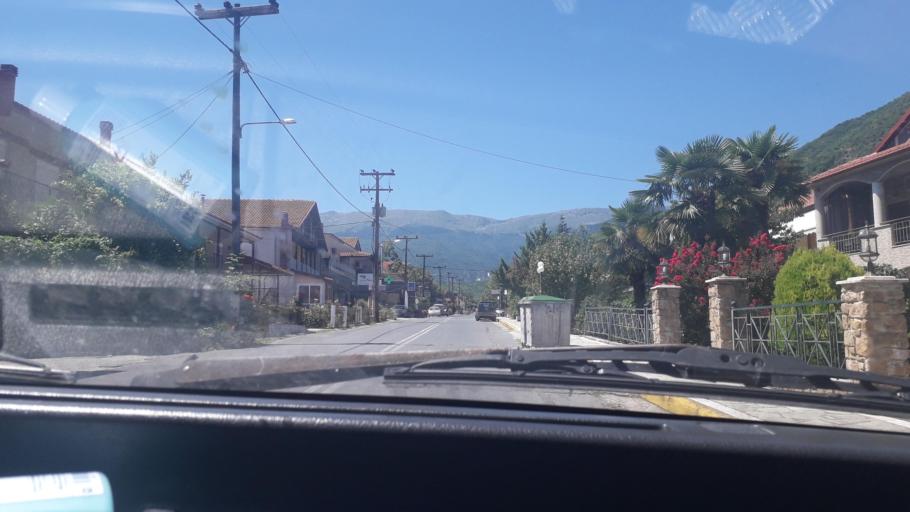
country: GR
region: Central Macedonia
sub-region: Nomos Pellis
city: Loutraki
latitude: 40.9698
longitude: 21.9477
